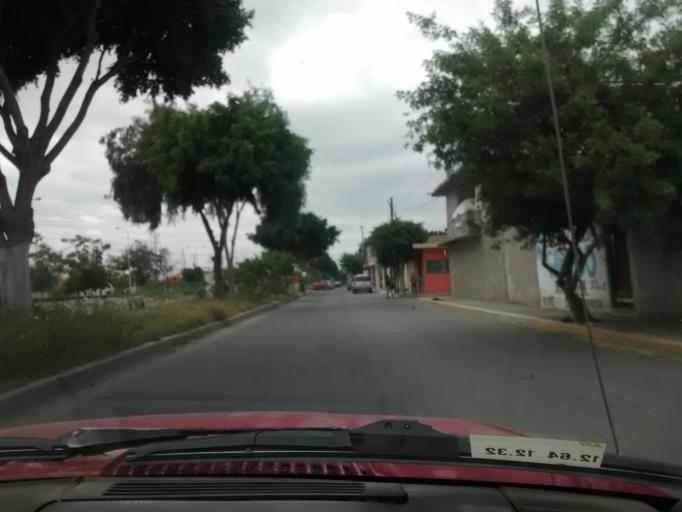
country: MX
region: Puebla
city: Tehuacan
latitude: 18.4765
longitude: -97.4093
